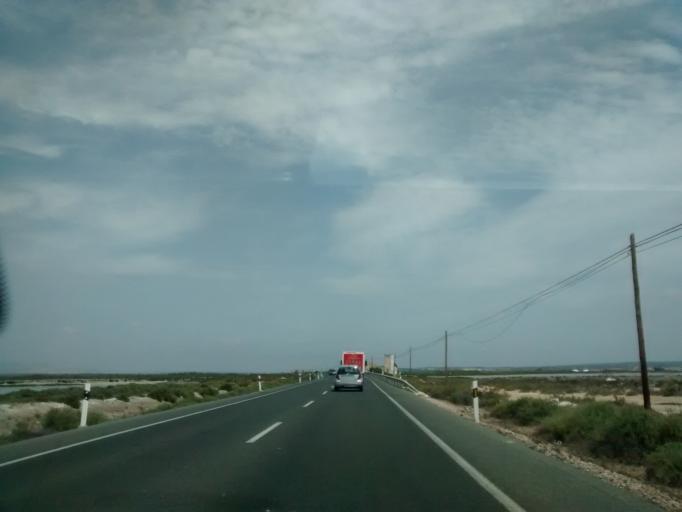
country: ES
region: Valencia
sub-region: Provincia de Alicante
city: Santa Pola
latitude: 38.1744
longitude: -0.6228
